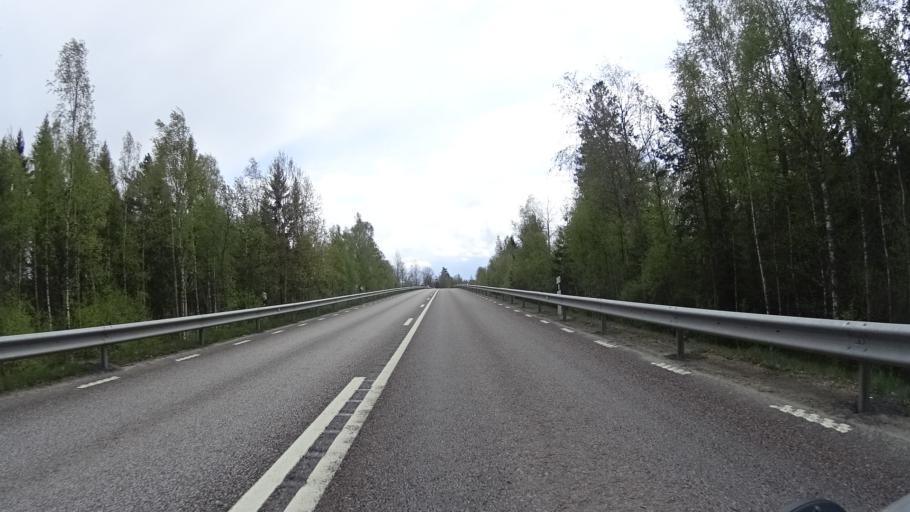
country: SE
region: Vaestra Goetaland
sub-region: Karlsborgs Kommun
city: Karlsborg
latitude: 58.5049
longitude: 14.4639
